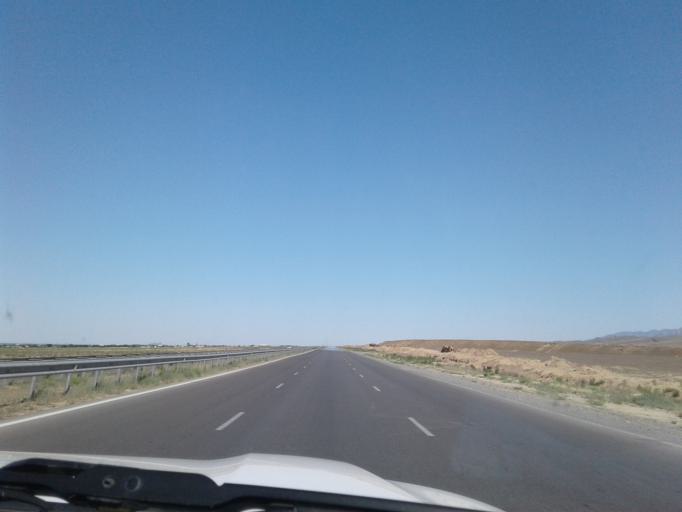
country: TM
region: Ahal
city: Annau
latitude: 37.7816
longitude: 58.8514
